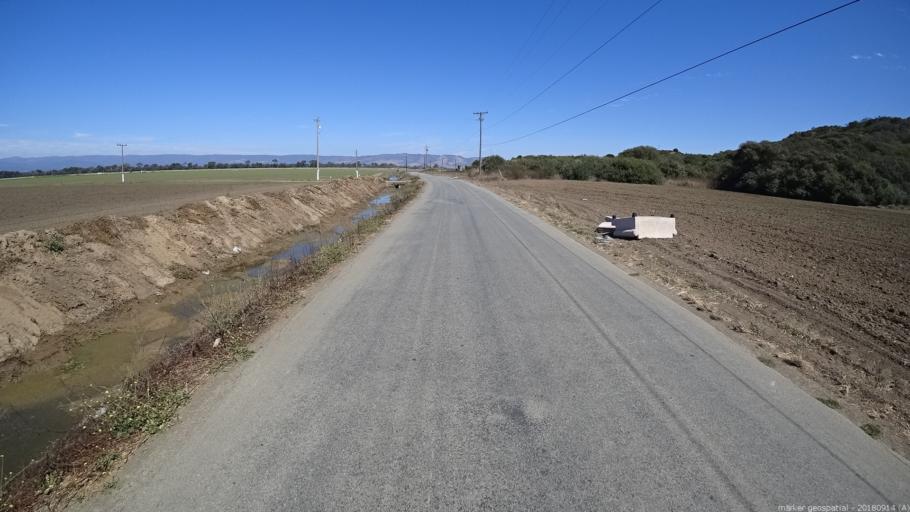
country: US
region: California
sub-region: Santa Cruz County
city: Watsonville
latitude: 36.8731
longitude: -121.7829
